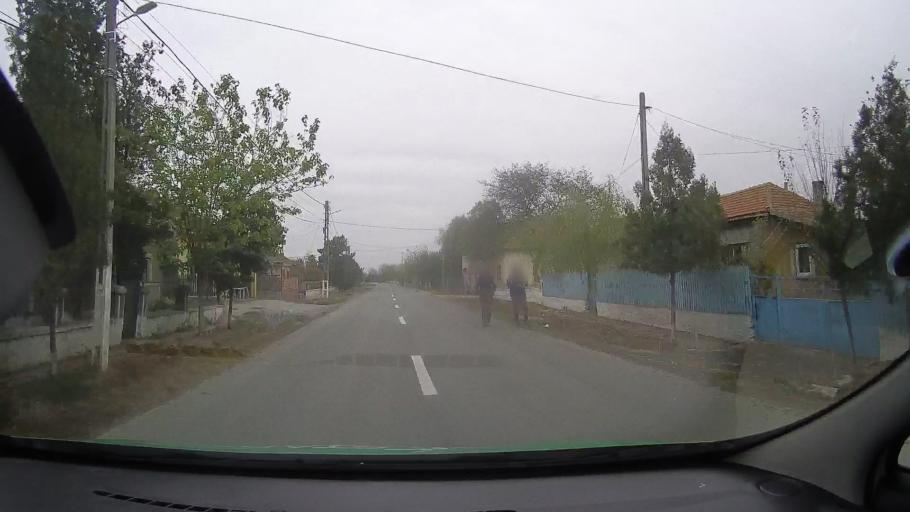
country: RO
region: Constanta
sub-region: Comuna Silistea
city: Silistea
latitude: 44.4446
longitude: 28.2365
